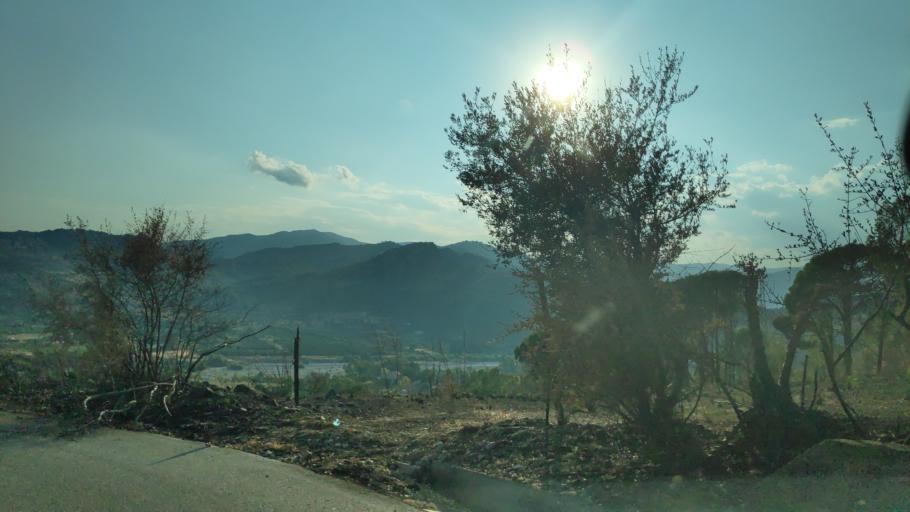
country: IT
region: Calabria
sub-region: Provincia di Reggio Calabria
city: Caulonia
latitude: 38.3970
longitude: 16.4292
